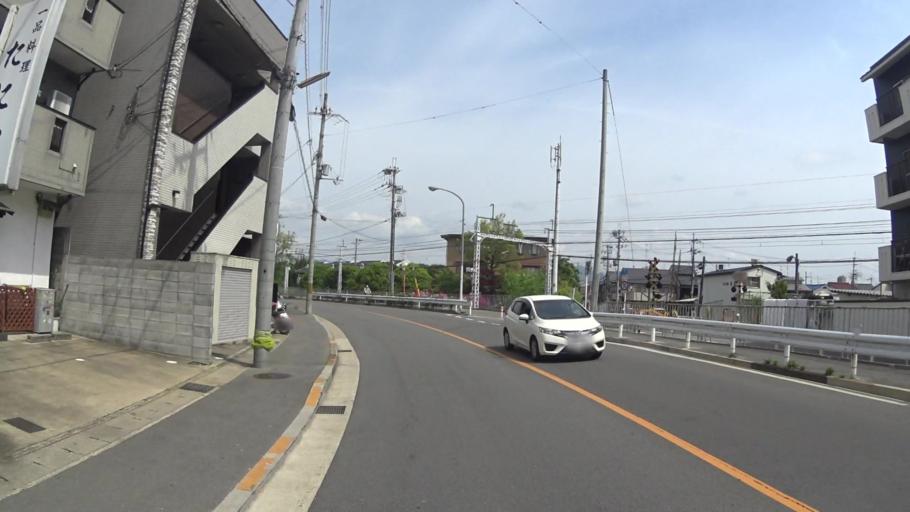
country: JP
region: Kyoto
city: Muko
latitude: 34.9923
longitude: 135.6929
